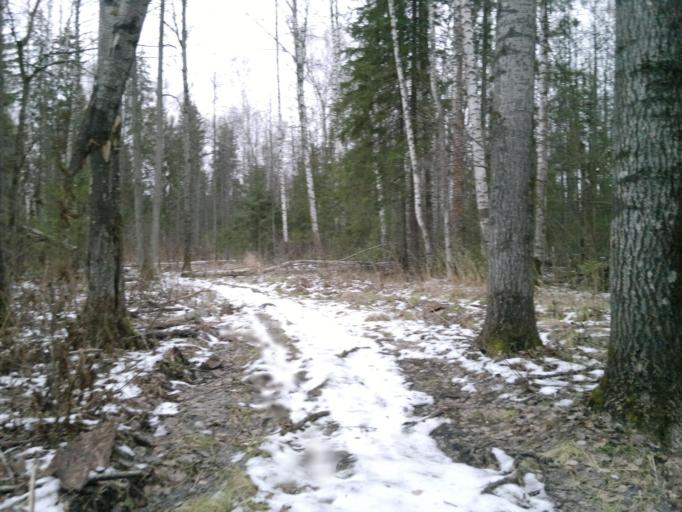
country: RU
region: Mariy-El
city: Yoshkar-Ola
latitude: 56.6095
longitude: 47.9497
